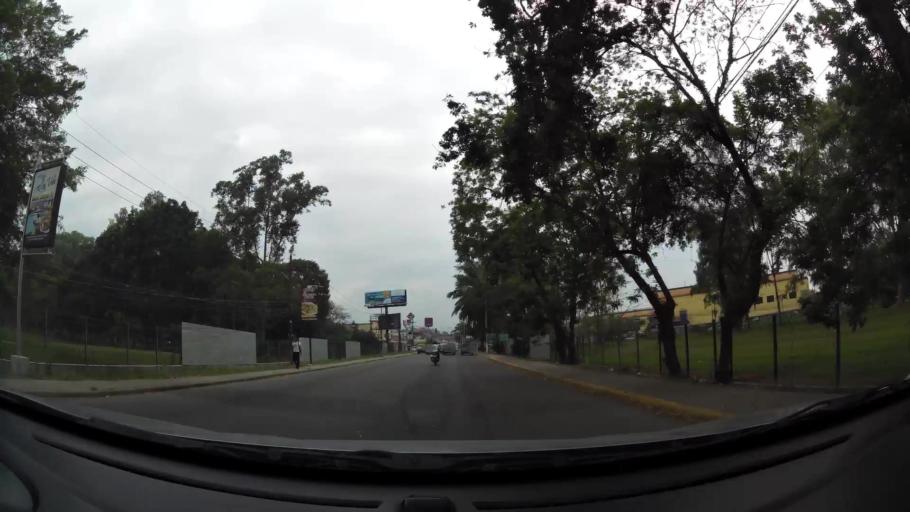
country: HN
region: Atlantida
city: La Ceiba
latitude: 15.7719
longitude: -86.7889
